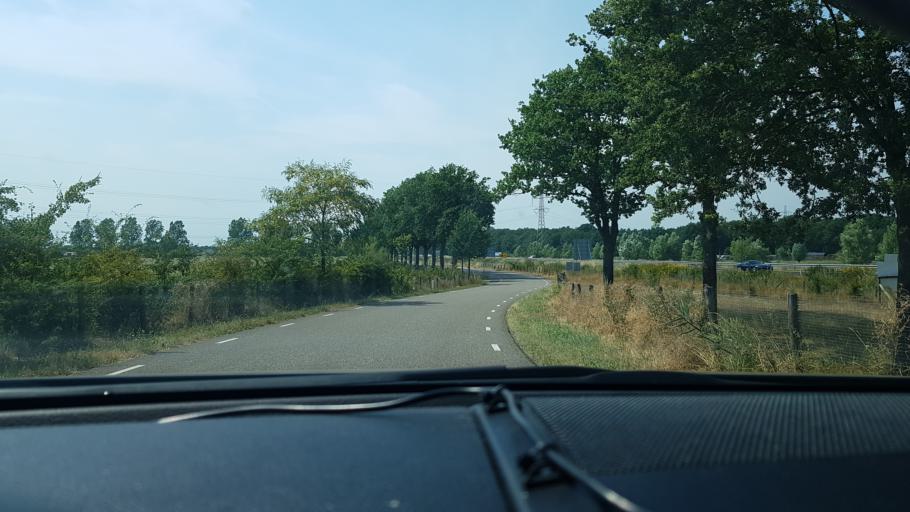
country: NL
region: Limburg
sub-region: Gemeente Roerdalen
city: Herkenbosch
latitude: 51.1991
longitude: 6.0598
